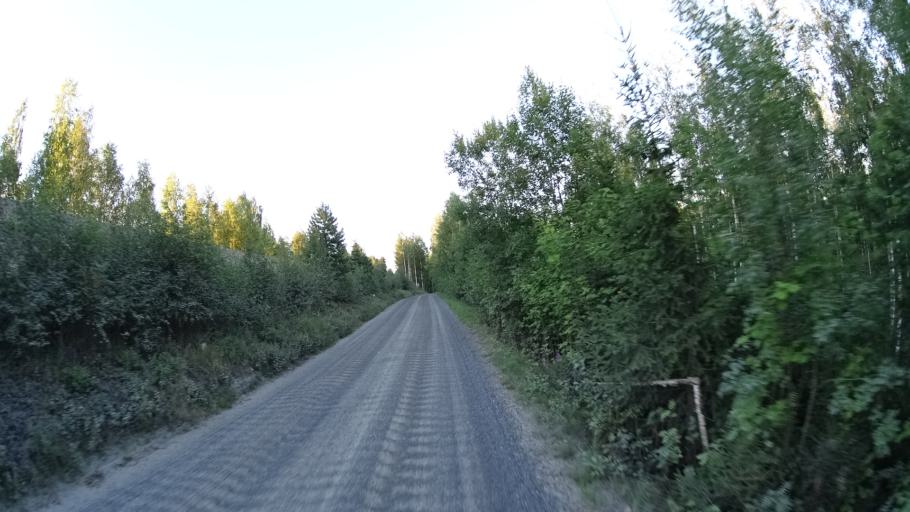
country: FI
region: Central Finland
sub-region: Jyvaeskylae
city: Petaejaevesi
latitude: 62.2556
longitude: 25.1768
